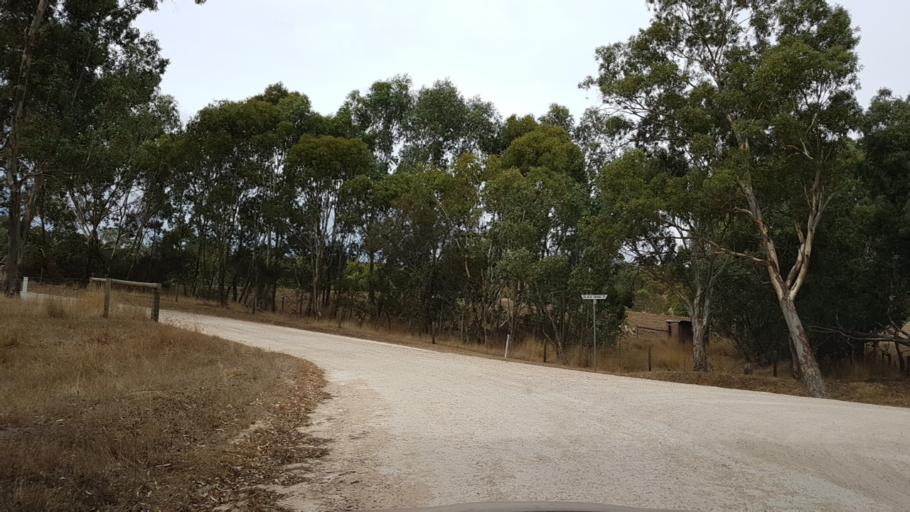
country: AU
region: South Australia
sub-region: Adelaide Hills
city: Birdwood
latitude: -34.7842
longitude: 138.9875
